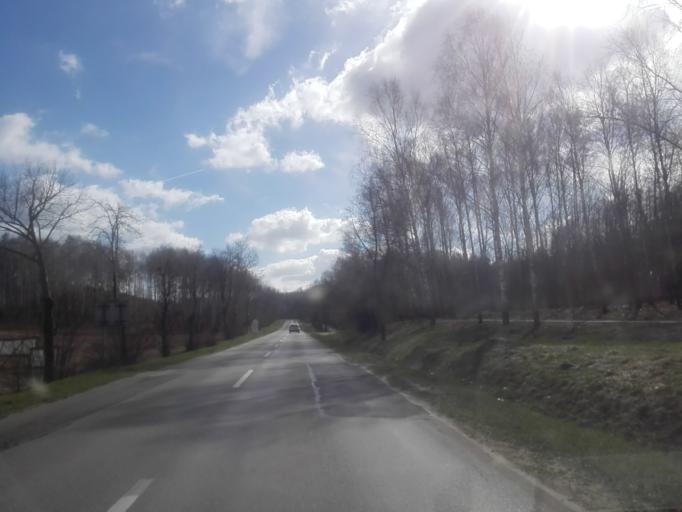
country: PL
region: Silesian Voivodeship
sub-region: Powiat czestochowski
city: Olsztyn
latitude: 50.7523
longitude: 19.2800
